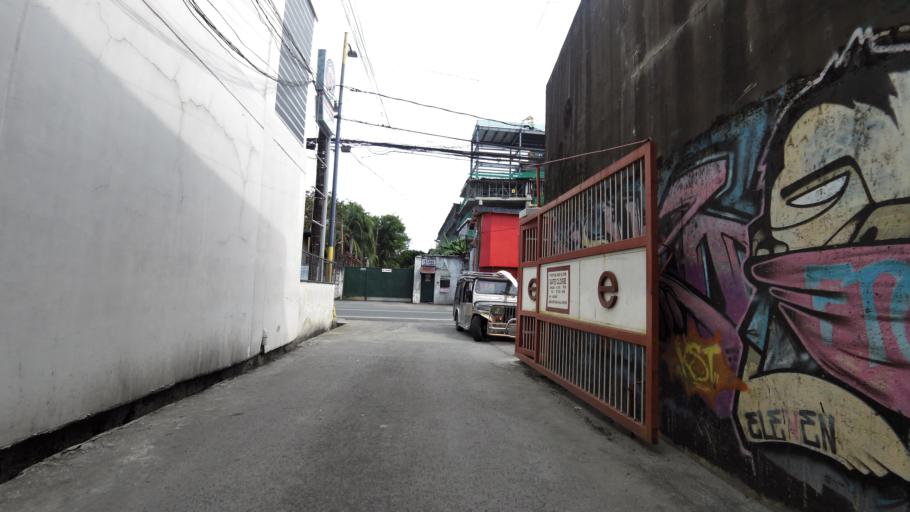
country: PH
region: Metro Manila
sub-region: Marikina
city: Calumpang
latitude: 14.6206
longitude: 121.0924
